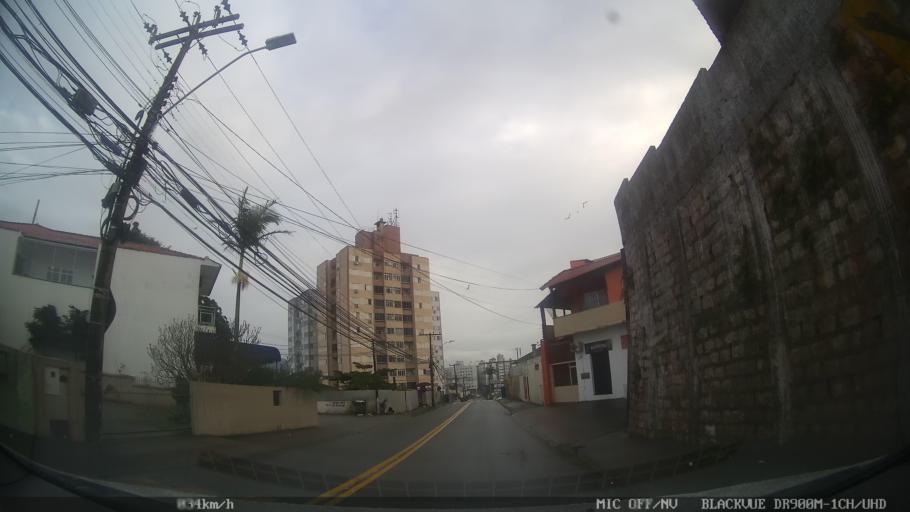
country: BR
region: Santa Catarina
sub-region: Sao Jose
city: Campinas
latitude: -27.5794
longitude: -48.6087
